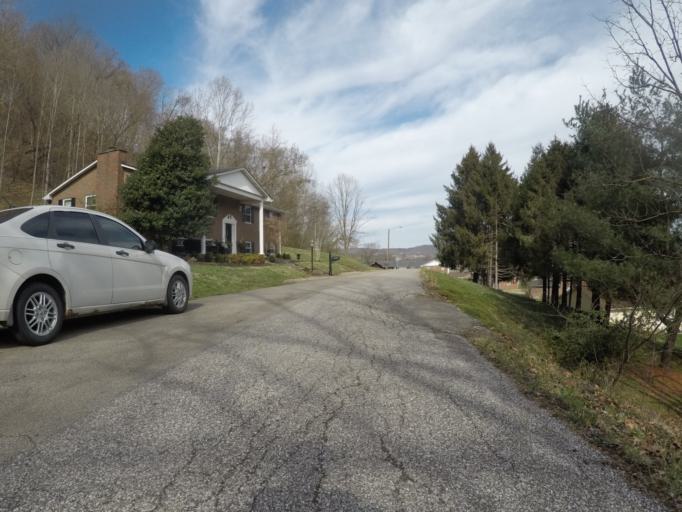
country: US
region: West Virginia
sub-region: Cabell County
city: Barboursville
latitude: 38.3976
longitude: -82.2945
